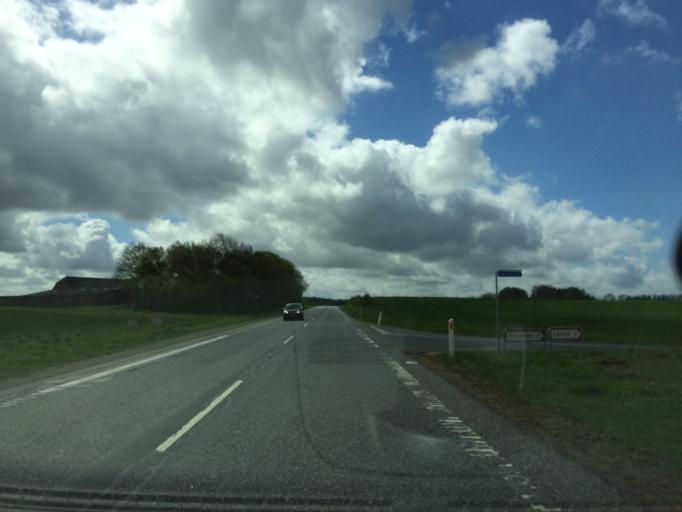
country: DK
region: Central Jutland
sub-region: Viborg Kommune
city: Stoholm
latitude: 56.4319
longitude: 9.1095
